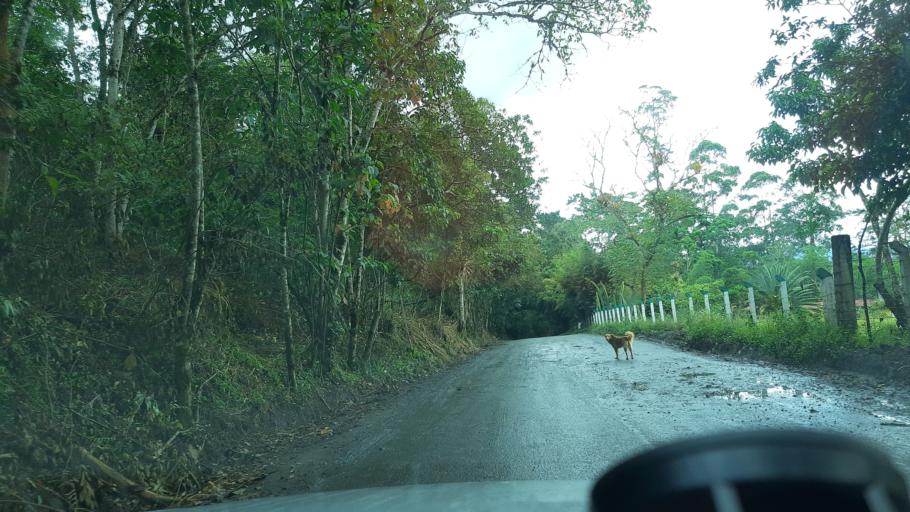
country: CO
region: Boyaca
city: Chinavita
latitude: 5.1368
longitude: -73.3623
